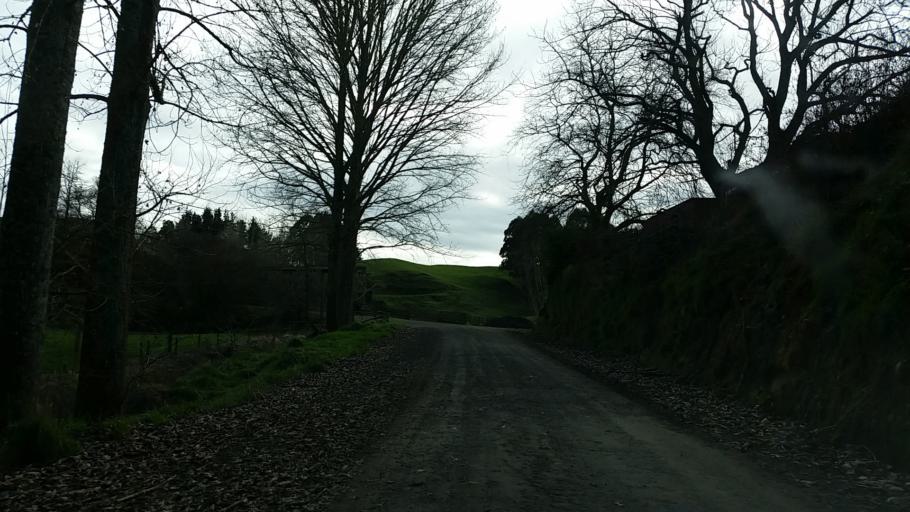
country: NZ
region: Taranaki
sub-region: South Taranaki District
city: Eltham
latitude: -39.2538
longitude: 174.5110
